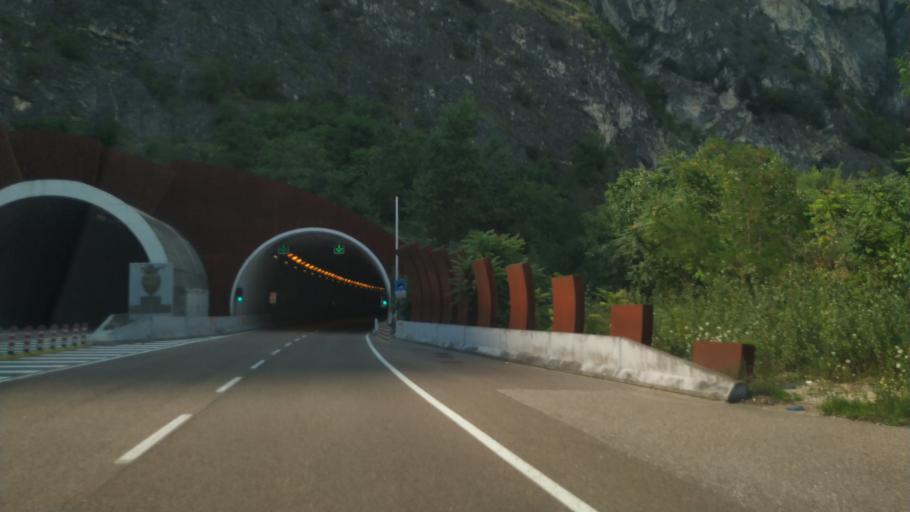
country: IT
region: Trentino-Alto Adige
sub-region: Provincia di Trento
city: Mezzolombardo
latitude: 46.1920
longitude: 11.0965
